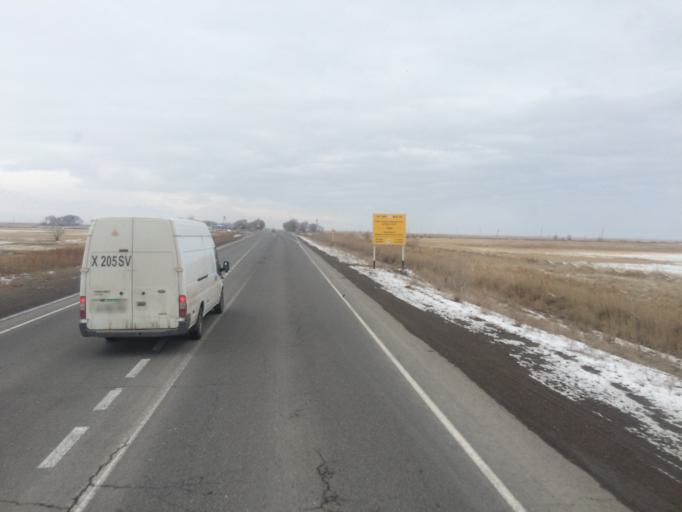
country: KG
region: Chuy
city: Tokmok
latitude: 43.3491
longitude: 75.4855
